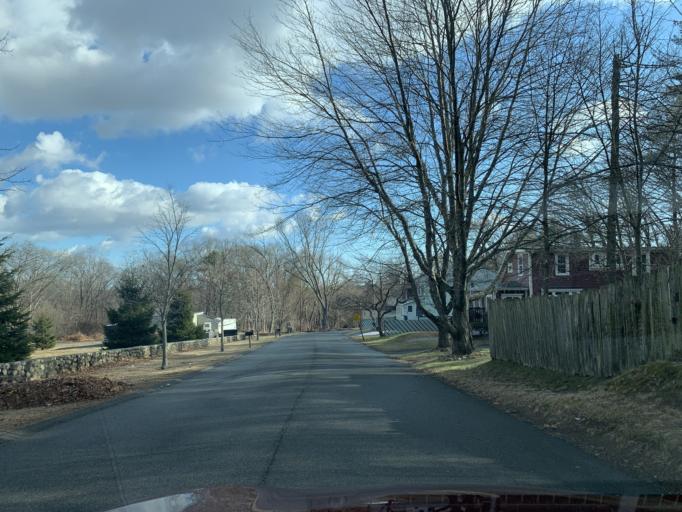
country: US
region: Massachusetts
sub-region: Essex County
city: Amesbury
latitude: 42.8430
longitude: -70.9331
